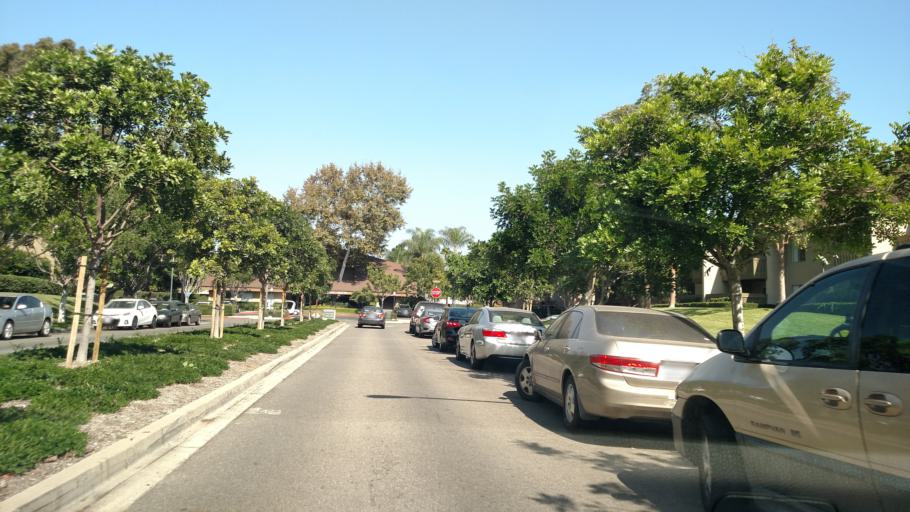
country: US
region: California
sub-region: Orange County
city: Irvine
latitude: 33.6678
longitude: -117.8275
